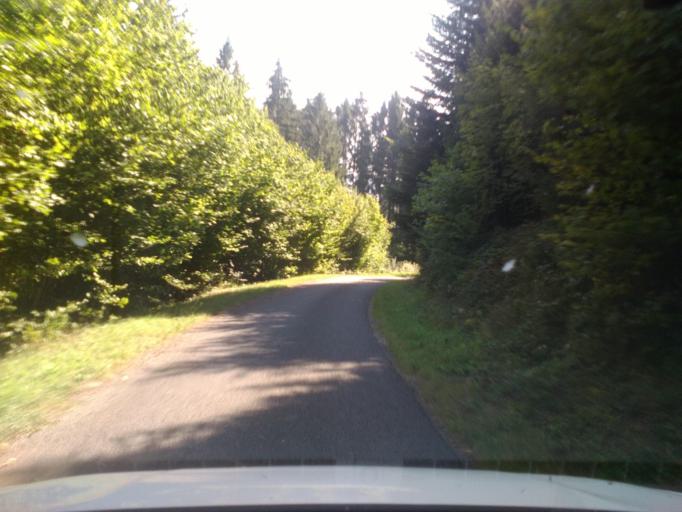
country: FR
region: Lorraine
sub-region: Departement des Vosges
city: Ban-de-Laveline
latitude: 48.3247
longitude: 7.0609
